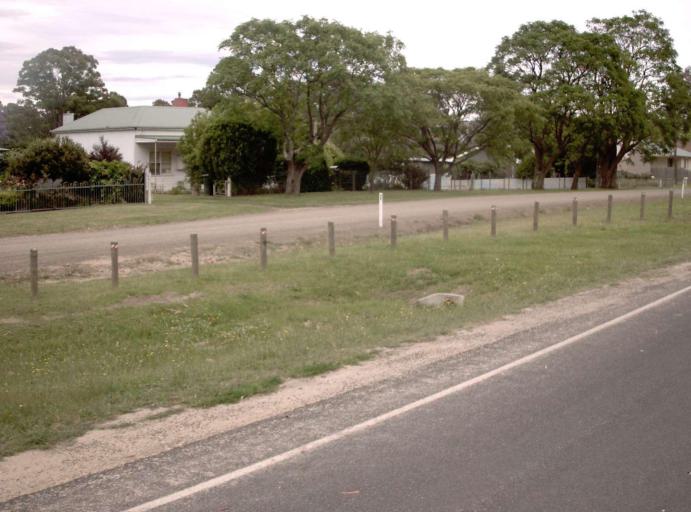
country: AU
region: Victoria
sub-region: East Gippsland
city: Bairnsdale
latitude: -37.8064
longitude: 147.6177
